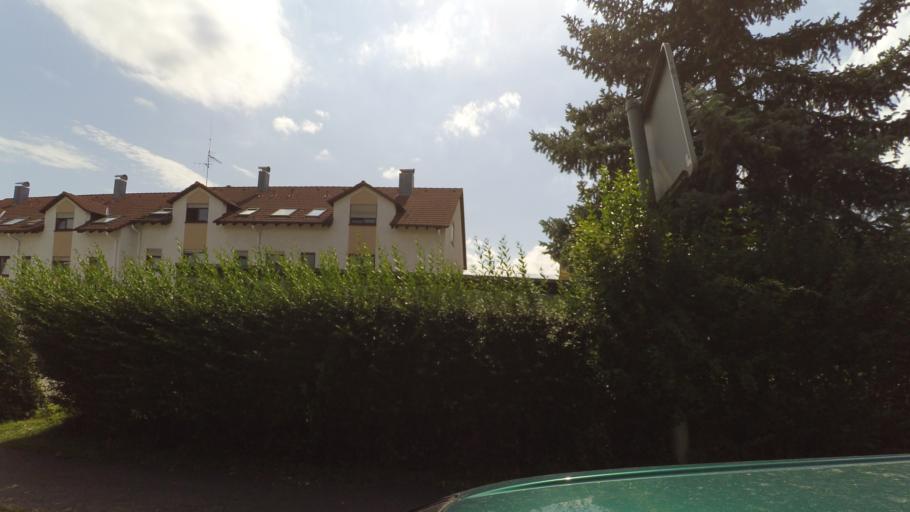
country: DE
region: Baden-Wuerttemberg
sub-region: Regierungsbezirk Stuttgart
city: Huttlingen
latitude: 48.8706
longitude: 10.1056
